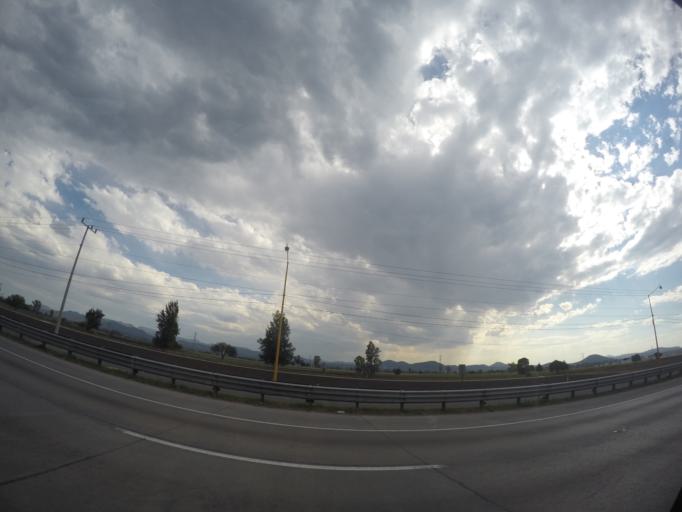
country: MX
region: Queretaro
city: La Estancia
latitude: 20.4236
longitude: -100.0525
